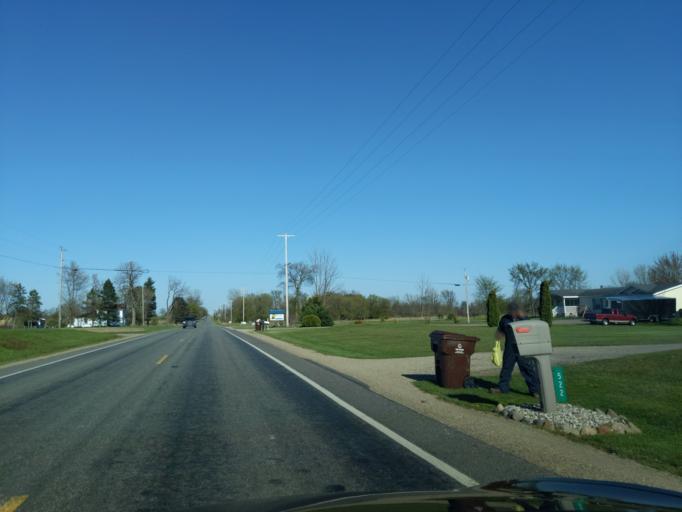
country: US
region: Michigan
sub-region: Ionia County
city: Ionia
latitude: 42.8860
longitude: -85.0636
